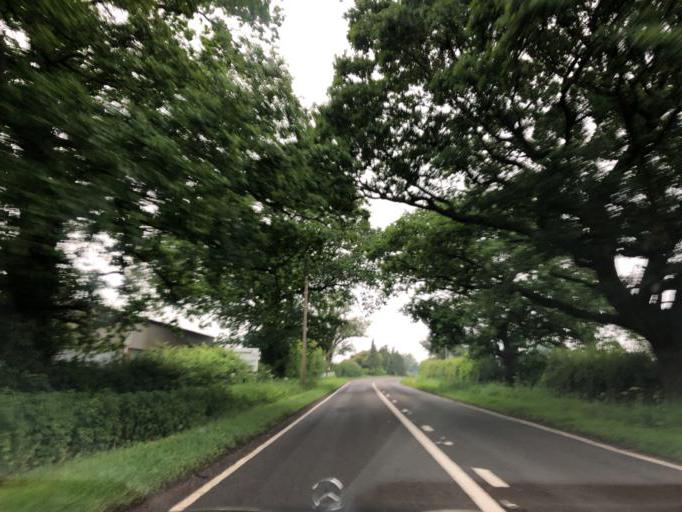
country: GB
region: England
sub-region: Warwickshire
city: Warwick
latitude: 52.2586
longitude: -1.5677
